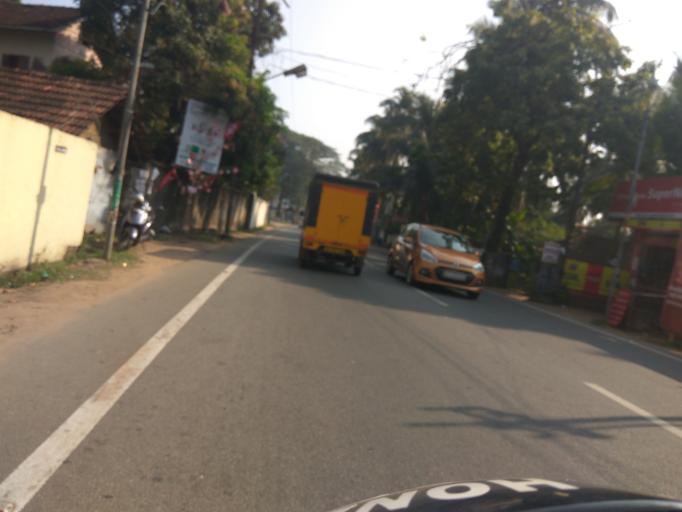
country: IN
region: Kerala
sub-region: Kozhikode
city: Kozhikode
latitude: 11.2795
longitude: 75.7709
